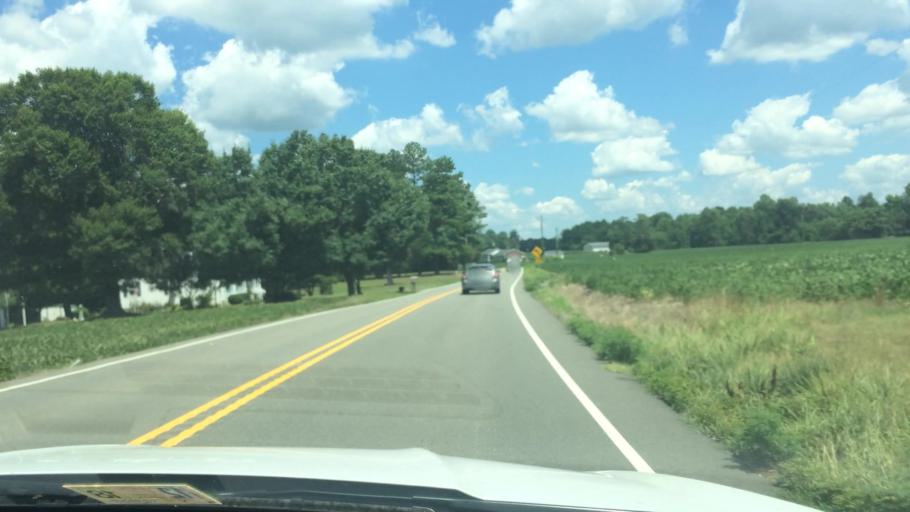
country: US
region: Virginia
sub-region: King William County
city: West Point
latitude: 37.5952
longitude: -76.7646
